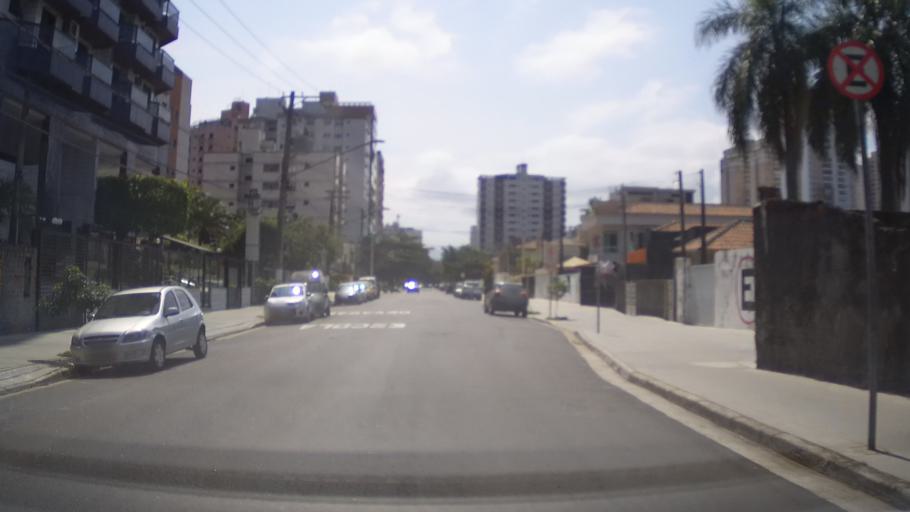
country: BR
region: Sao Paulo
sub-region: Guaruja
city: Guaruja
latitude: -23.9866
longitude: -46.2965
